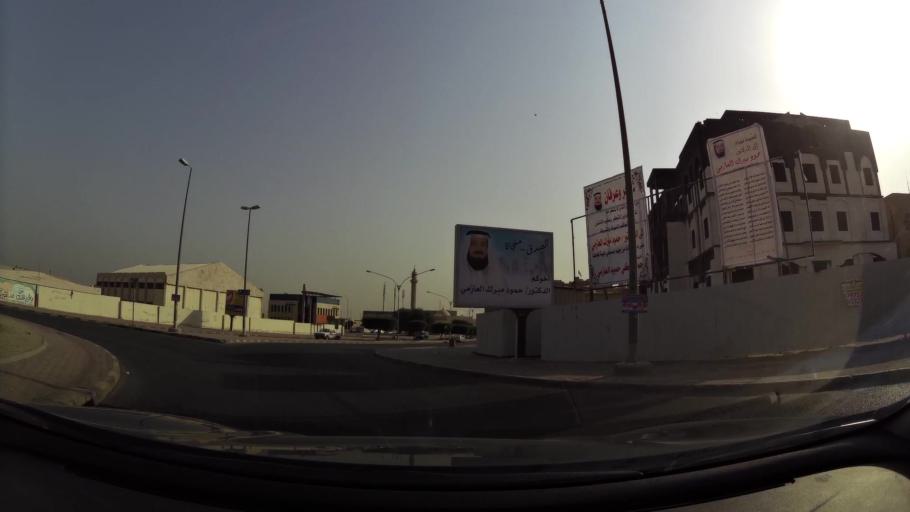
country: KW
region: Al Ahmadi
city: Al Manqaf
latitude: 29.1049
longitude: 48.1051
